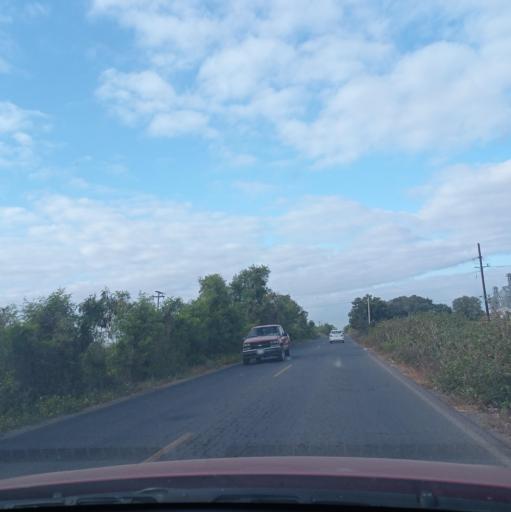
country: MX
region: Sinaloa
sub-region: Guasave
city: Las Quemazones
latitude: 25.6530
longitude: -108.5266
